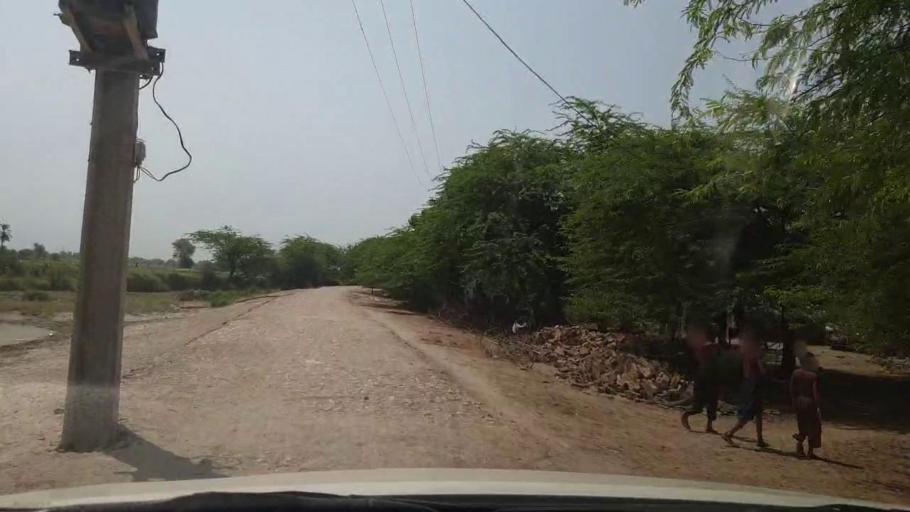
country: PK
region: Sindh
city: Shikarpur
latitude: 27.9870
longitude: 68.7164
